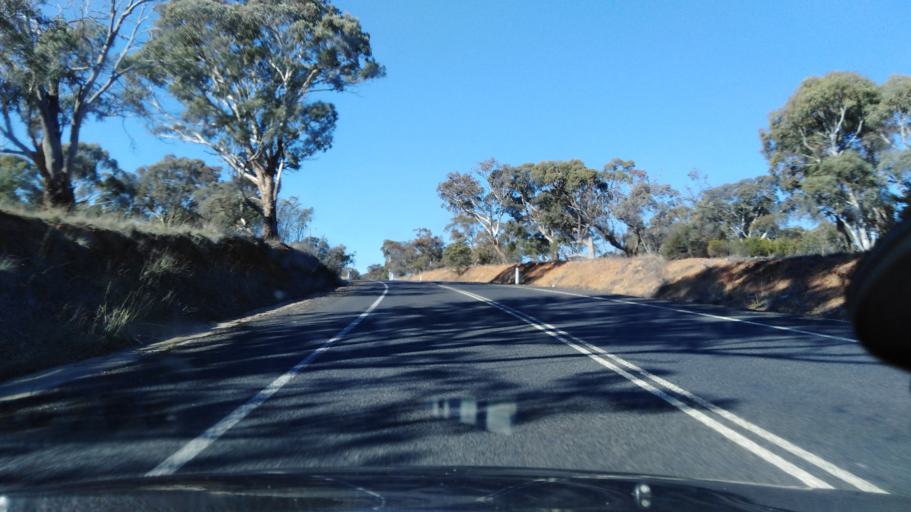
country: AU
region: New South Wales
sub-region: Yass Valley
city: Gundaroo
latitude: -35.1816
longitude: 149.2736
